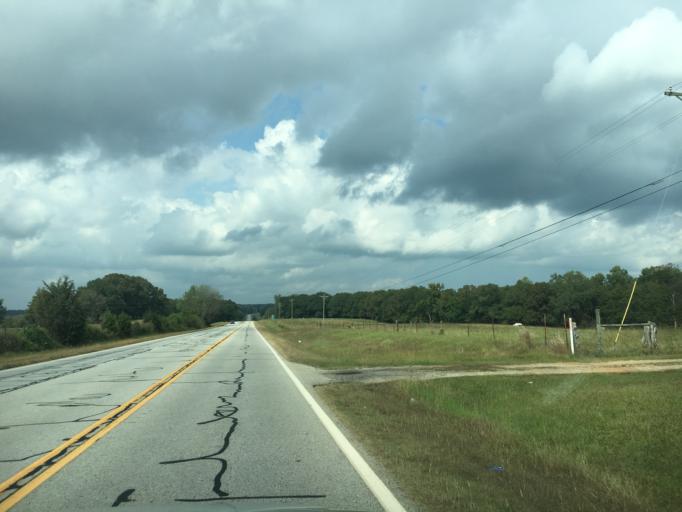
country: US
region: Georgia
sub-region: Hart County
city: Hartwell
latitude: 34.2372
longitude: -82.8979
